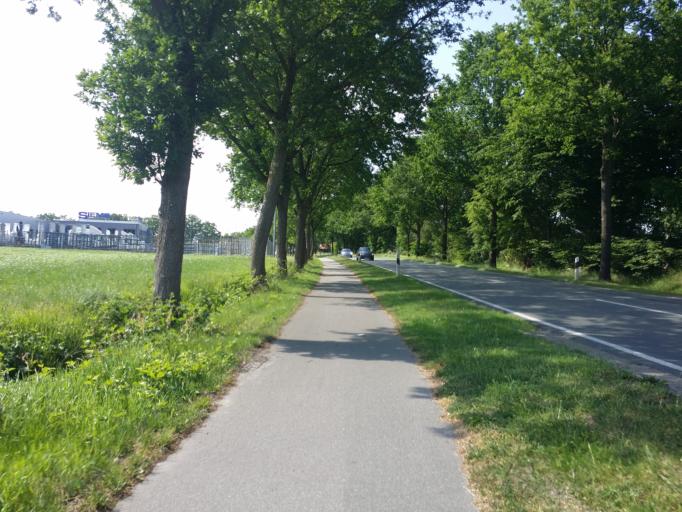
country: DE
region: Lower Saxony
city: Wiefelstede
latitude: 53.2467
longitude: 8.1287
